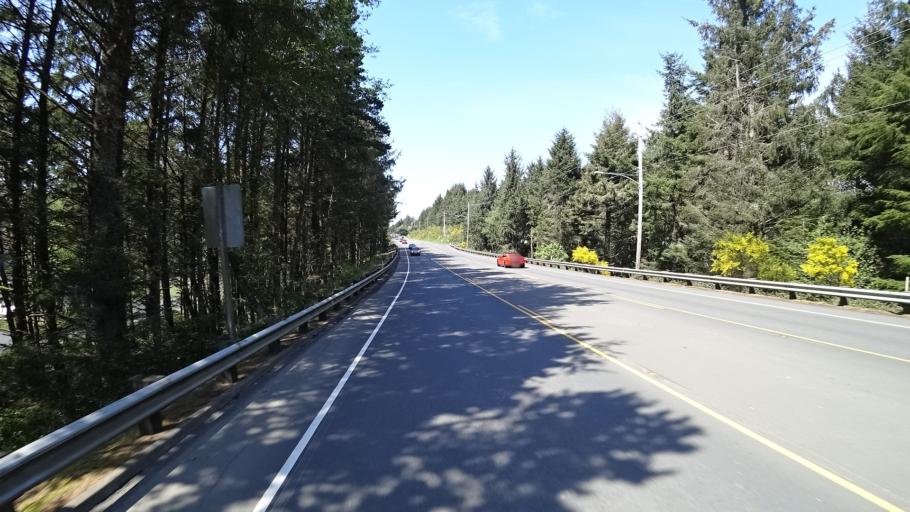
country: US
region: Oregon
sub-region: Lincoln County
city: Newport
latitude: 44.6590
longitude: -124.0537
